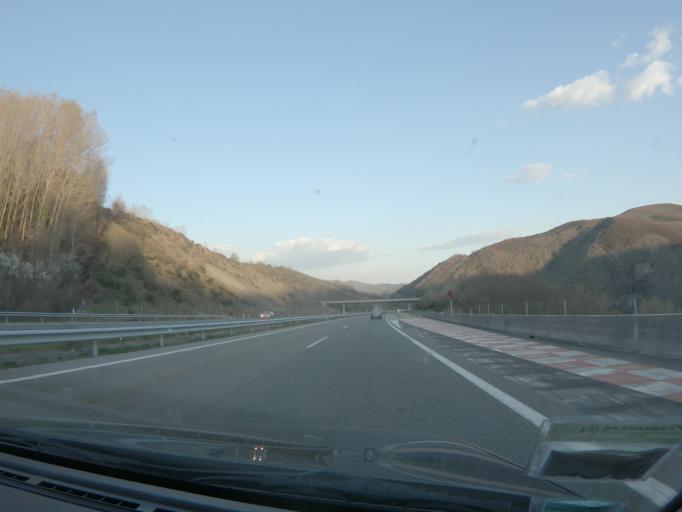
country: ES
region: Castille and Leon
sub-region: Provincia de Leon
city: Vega de Valcarce
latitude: 42.6688
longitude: -6.9489
